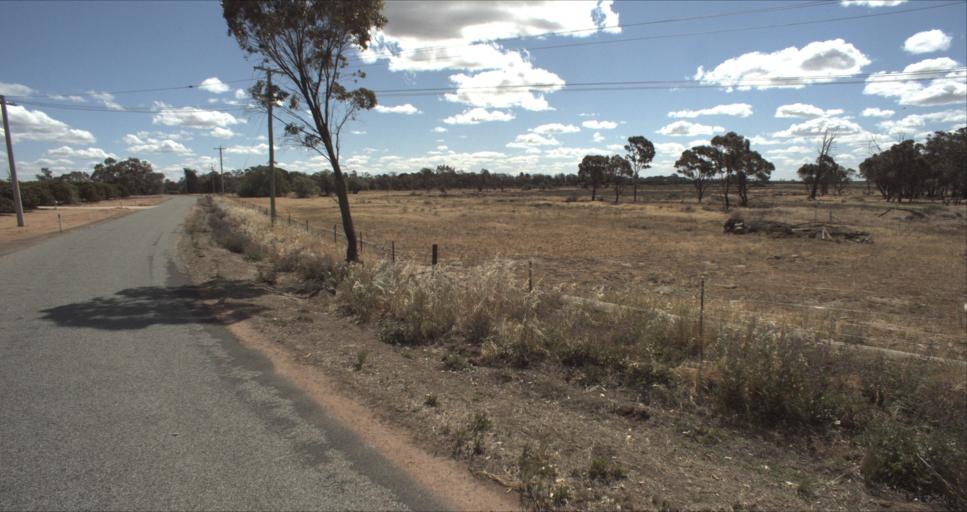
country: AU
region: New South Wales
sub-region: Leeton
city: Leeton
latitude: -34.5180
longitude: 146.2279
